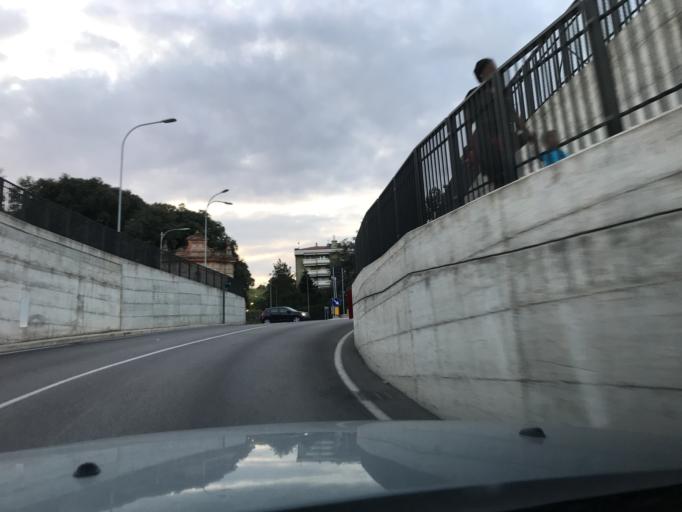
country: IT
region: Umbria
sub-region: Provincia di Perugia
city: Ponte Felcino
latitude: 43.0887
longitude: 12.4299
